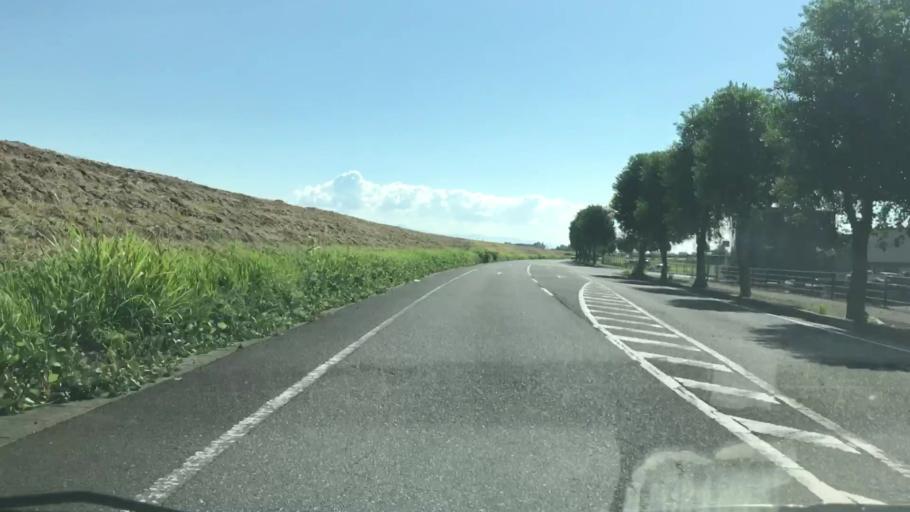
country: JP
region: Saga Prefecture
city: Okawa
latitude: 33.2292
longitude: 130.3749
